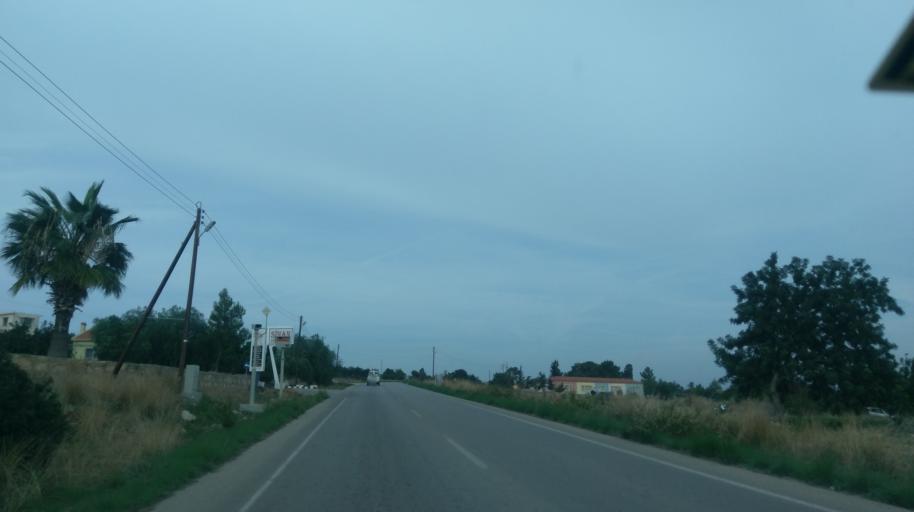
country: CY
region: Ammochostos
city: Leonarisso
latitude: 35.4223
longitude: 34.1258
